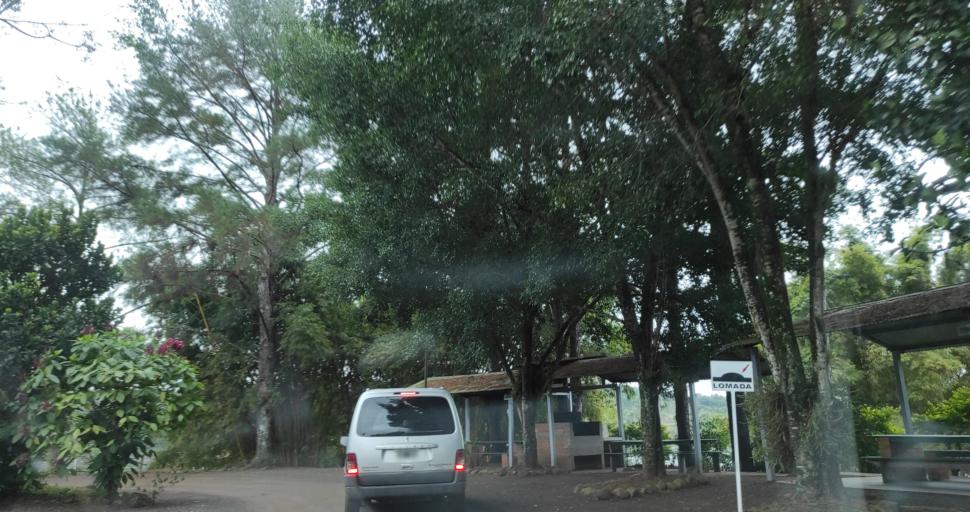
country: AR
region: Misiones
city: Puerto Rico
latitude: -26.7913
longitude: -55.0144
